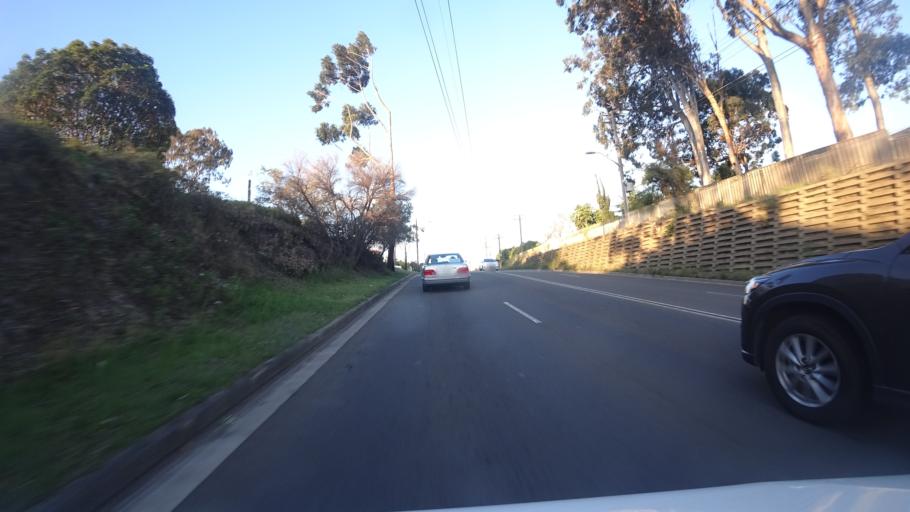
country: AU
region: New South Wales
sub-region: Ryde
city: North Ryde
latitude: -33.8019
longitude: 151.1160
